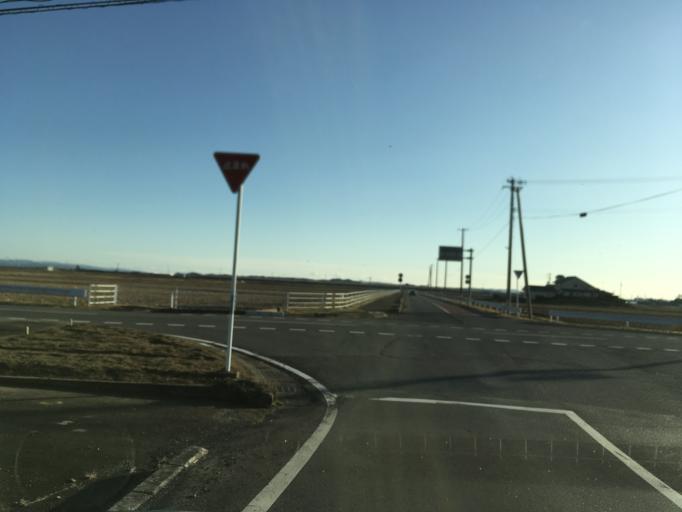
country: JP
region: Iwate
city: Ichinoseki
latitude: 38.7519
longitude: 141.1644
